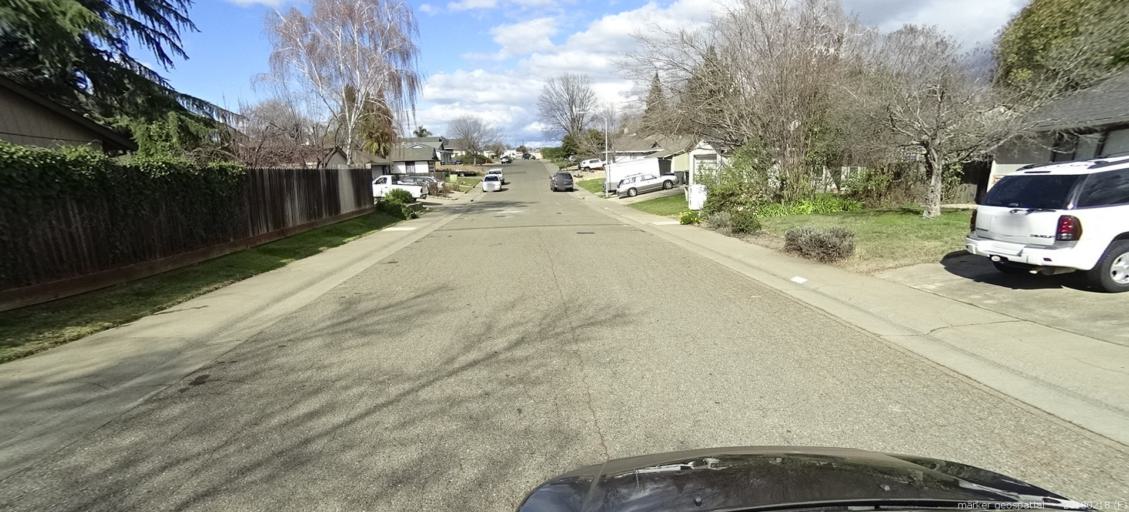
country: US
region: California
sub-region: Sacramento County
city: Orangevale
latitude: 38.6742
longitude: -121.2053
